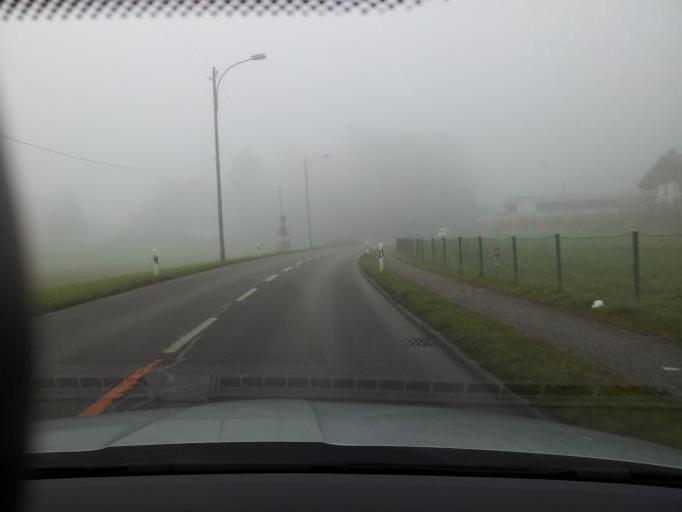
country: CH
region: Lucerne
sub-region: Lucerne-Stadt District
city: Littau
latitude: 47.0345
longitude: 8.2547
